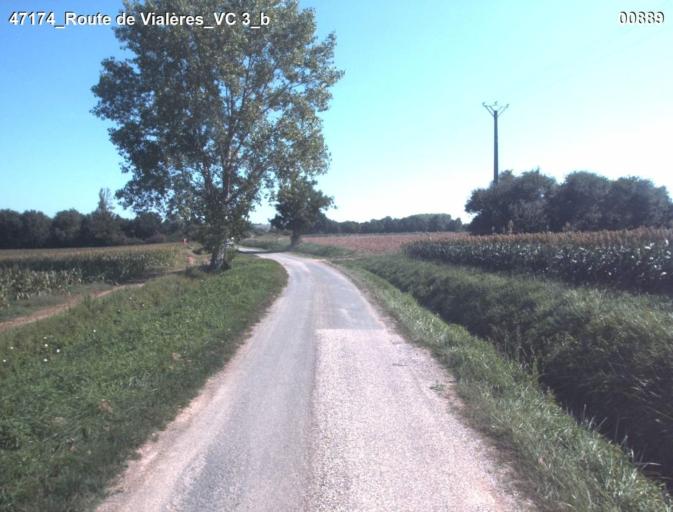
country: FR
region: Midi-Pyrenees
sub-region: Departement du Gers
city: Condom
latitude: 44.0424
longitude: 0.3753
